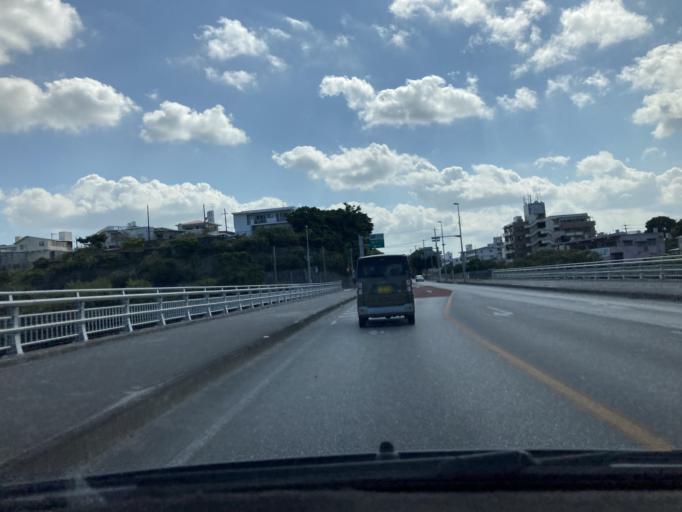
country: JP
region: Okinawa
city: Tomigusuku
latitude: 26.1720
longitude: 127.6911
